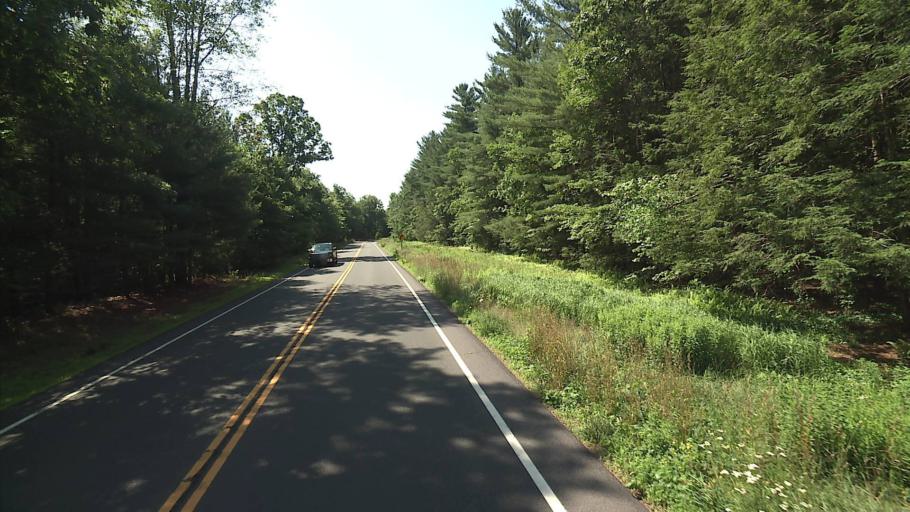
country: US
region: Connecticut
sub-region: Litchfield County
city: Terryville
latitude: 41.7094
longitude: -73.0112
